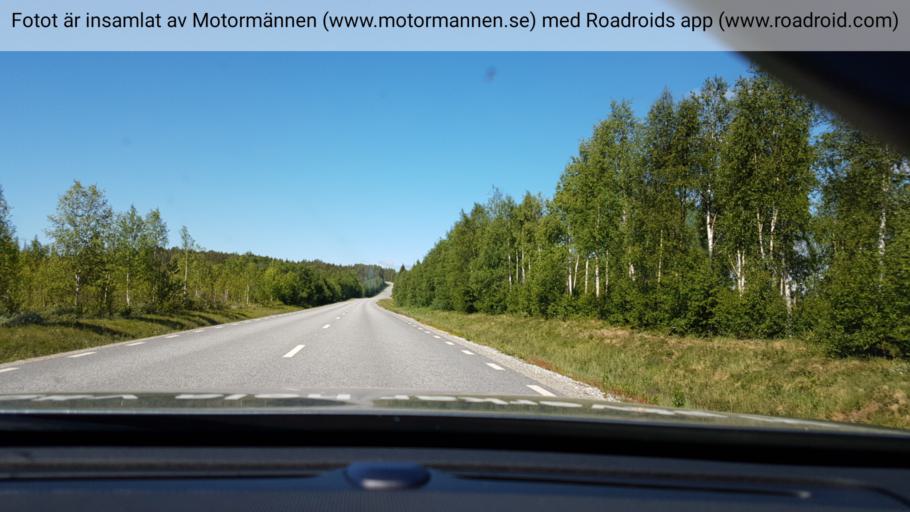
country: SE
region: Vaesterbotten
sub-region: Asele Kommun
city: Asele
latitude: 64.1996
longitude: 17.5378
